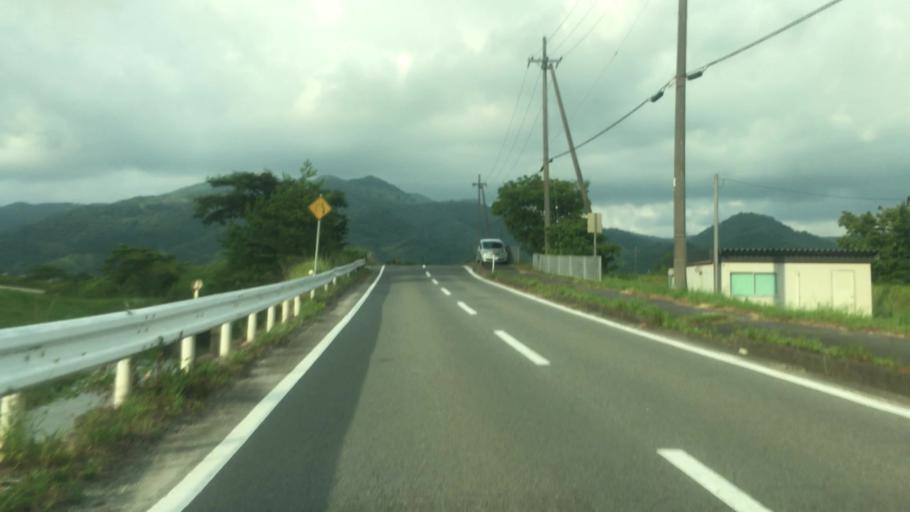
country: JP
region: Hyogo
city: Toyooka
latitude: 35.5641
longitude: 134.8046
